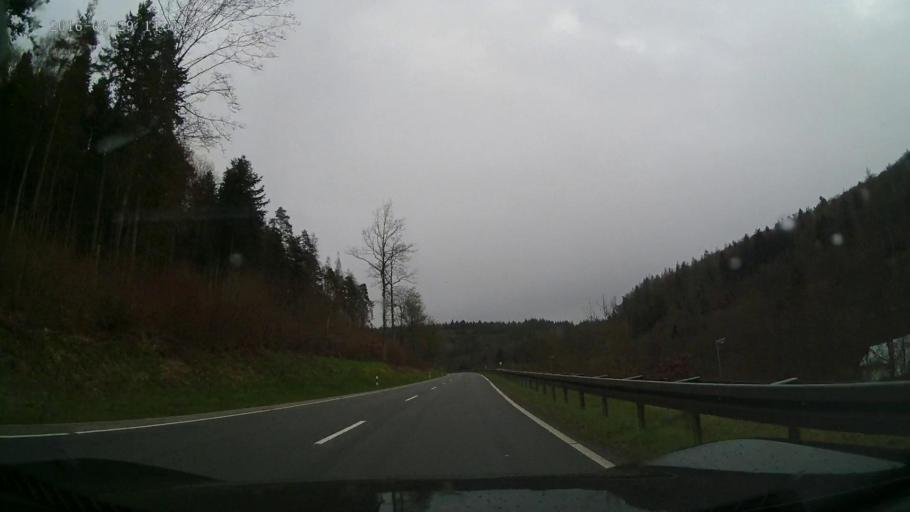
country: DE
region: Baden-Wuerttemberg
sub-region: Karlsruhe Region
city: Walldurn
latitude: 49.6046
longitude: 9.3403
